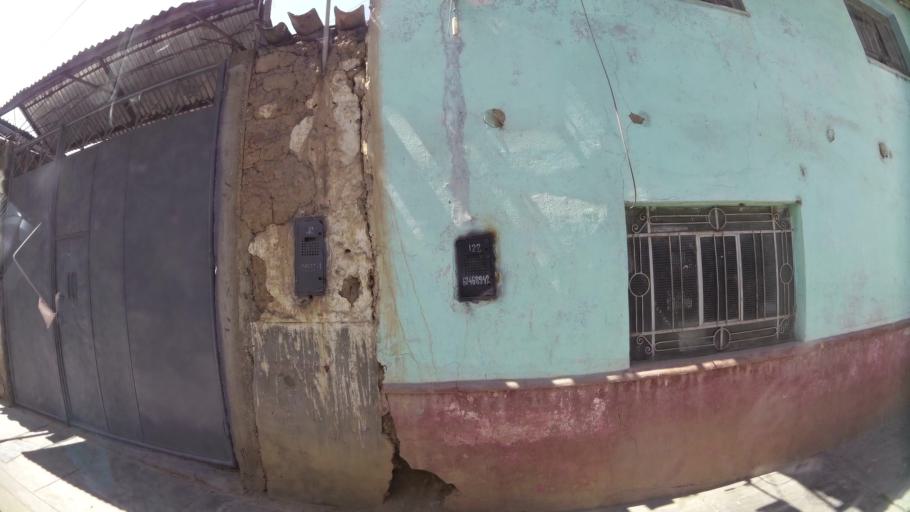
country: PE
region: Junin
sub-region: Provincia de Huancayo
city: El Tambo
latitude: -12.0861
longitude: -75.2112
